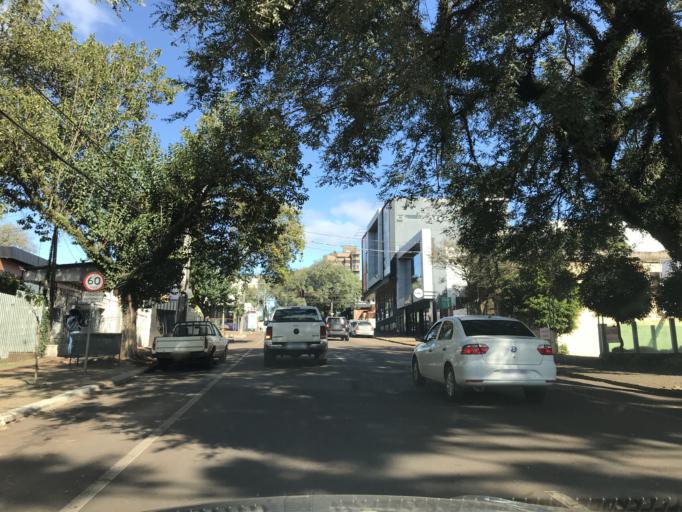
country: BR
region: Parana
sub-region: Cascavel
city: Cascavel
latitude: -24.9528
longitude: -53.4692
